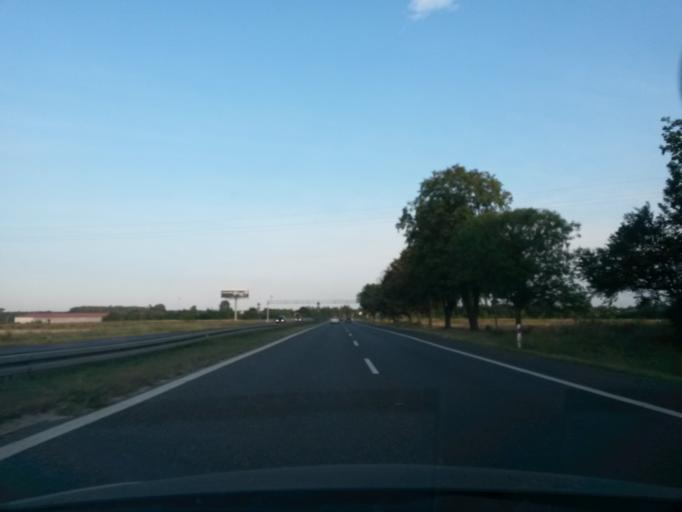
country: PL
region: Masovian Voivodeship
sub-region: Powiat plonski
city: Zaluski
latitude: 52.4804
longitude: 20.5586
